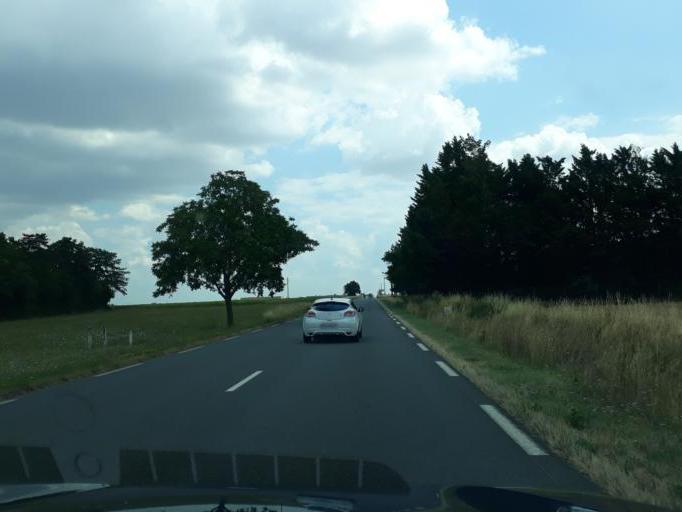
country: FR
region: Centre
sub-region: Departement du Cher
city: Avord
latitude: 47.0337
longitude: 2.6301
